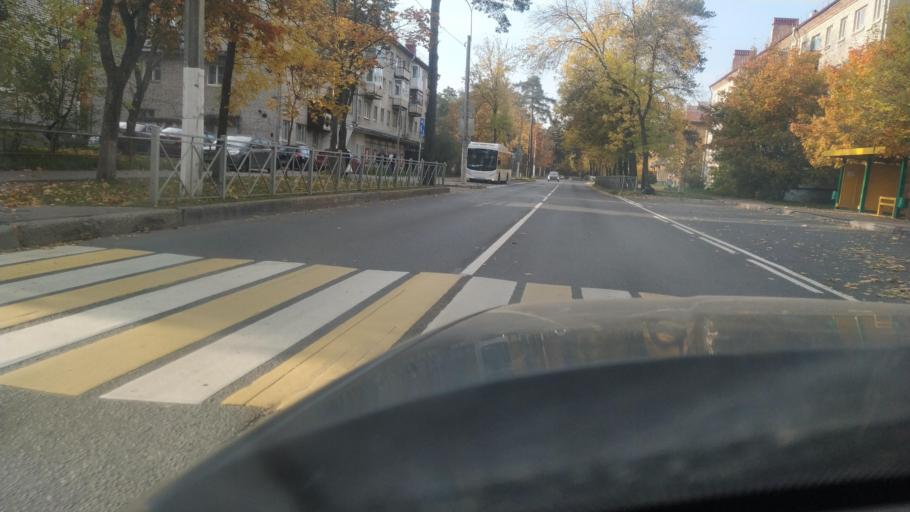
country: RU
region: Leningrad
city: Sosnovyy Bor
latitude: 59.8894
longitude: 29.0907
